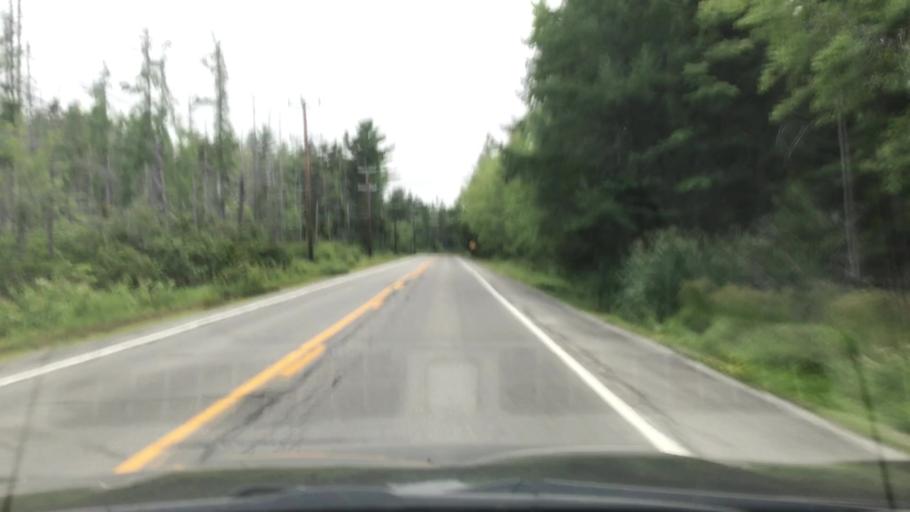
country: US
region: Maine
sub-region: Hancock County
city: Trenton
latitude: 44.4100
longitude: -68.3534
